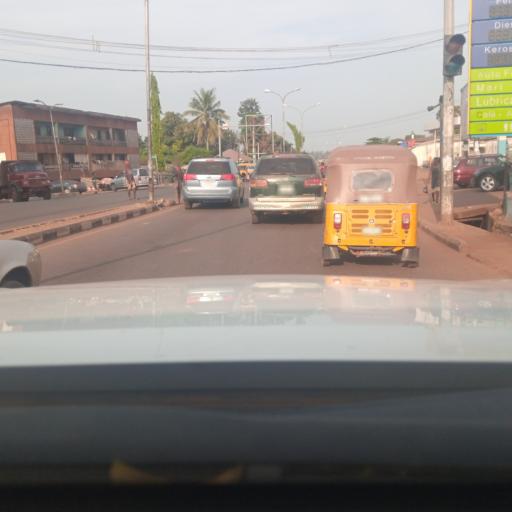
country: NG
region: Enugu
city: Enugu
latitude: 6.4529
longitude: 7.5041
